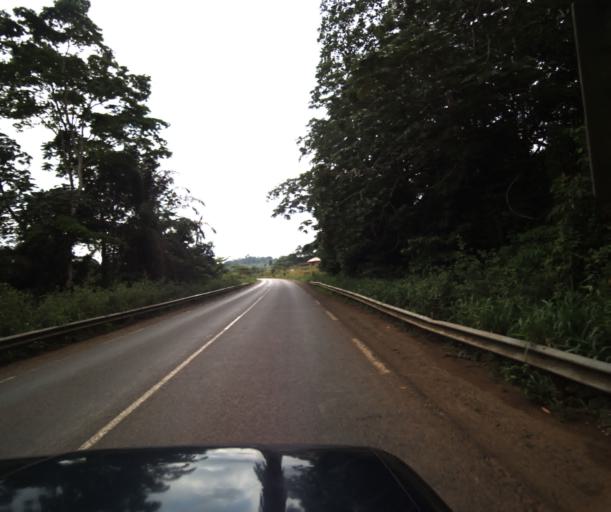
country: CM
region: Centre
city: Eseka
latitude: 3.8926
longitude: 10.7194
